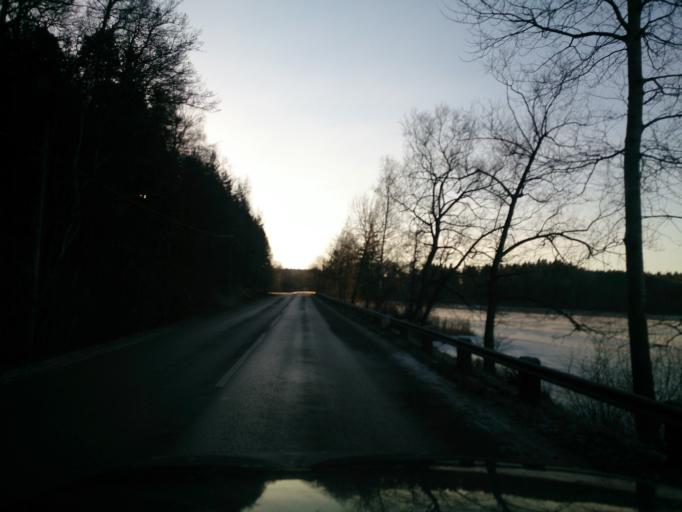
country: SE
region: OEstergoetland
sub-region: Atvidabergs Kommun
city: Atvidaberg
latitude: 58.3426
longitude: 16.0267
